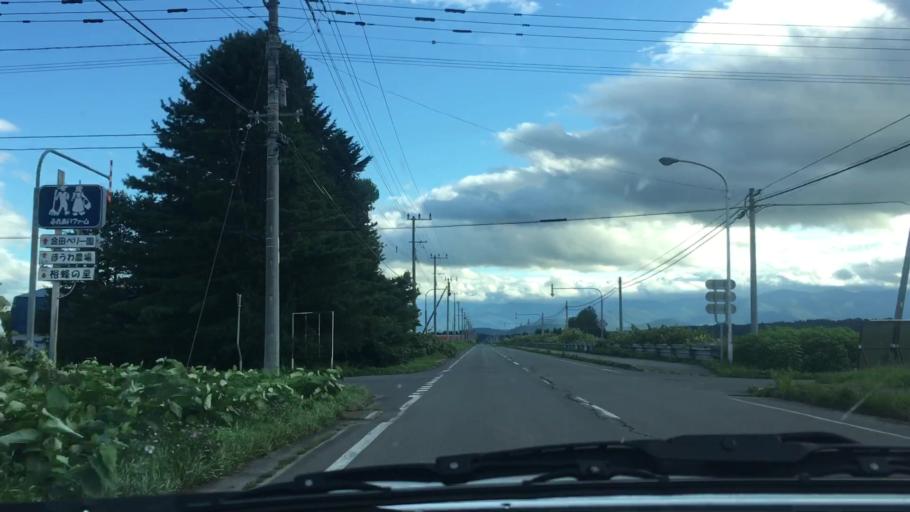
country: JP
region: Hokkaido
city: Otofuke
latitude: 43.1538
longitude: 142.9014
